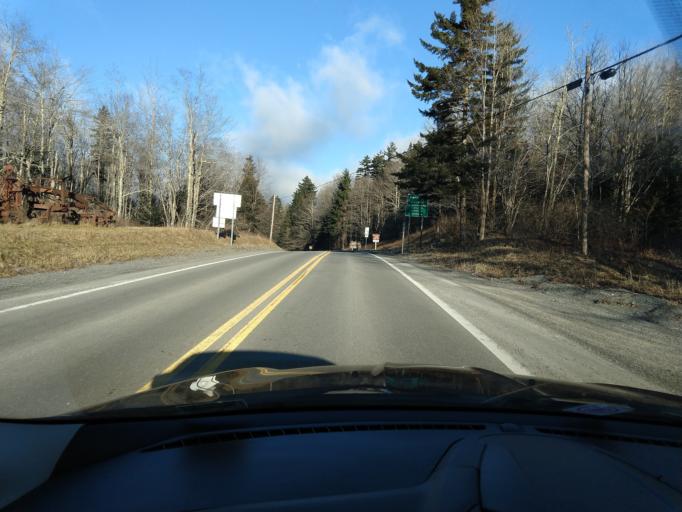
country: US
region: Virginia
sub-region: Highland County
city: Monterey
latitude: 38.5986
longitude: -79.8490
